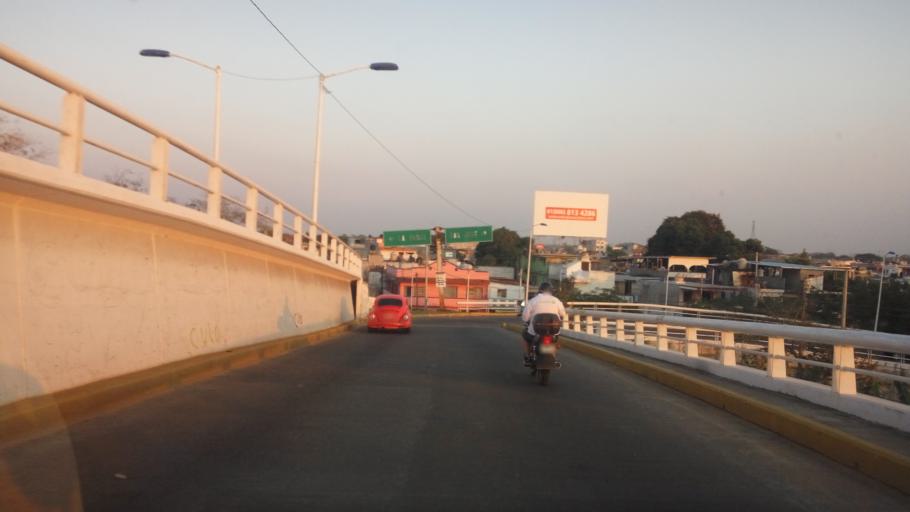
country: MX
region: Tabasco
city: Villahermosa
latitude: 17.9830
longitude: -92.9208
